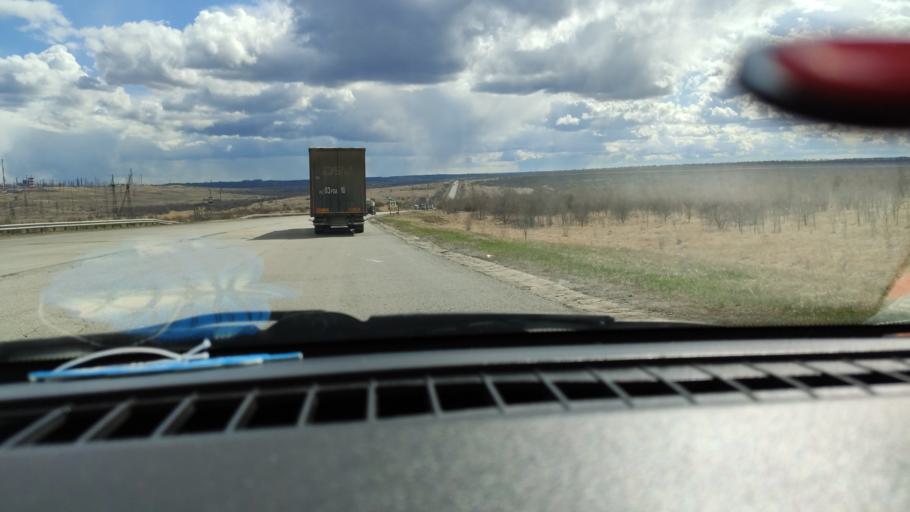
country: RU
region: Samara
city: Varlamovo
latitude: 53.1025
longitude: 48.3565
